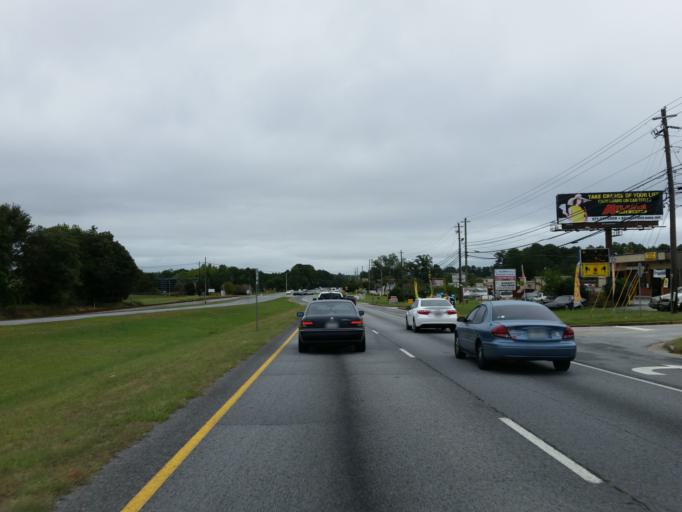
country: US
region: Georgia
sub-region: Clayton County
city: Bonanza
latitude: 33.4786
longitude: -84.3383
